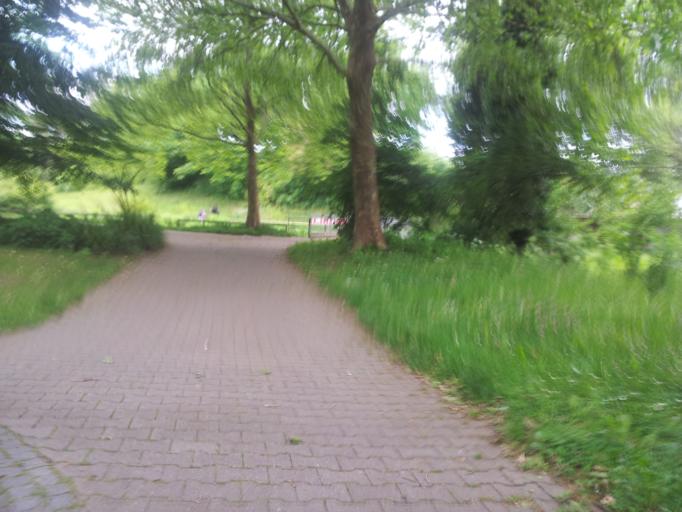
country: DE
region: Baden-Wuerttemberg
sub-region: Regierungsbezirk Stuttgart
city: Esslingen
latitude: 48.7344
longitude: 9.3118
